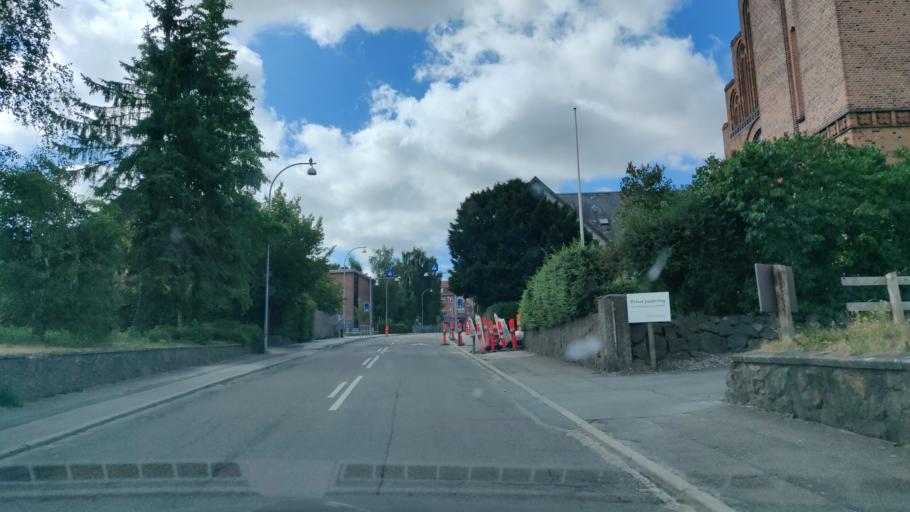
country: DK
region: Zealand
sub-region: Roskilde Kommune
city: Roskilde
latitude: 55.6449
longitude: 12.0836
